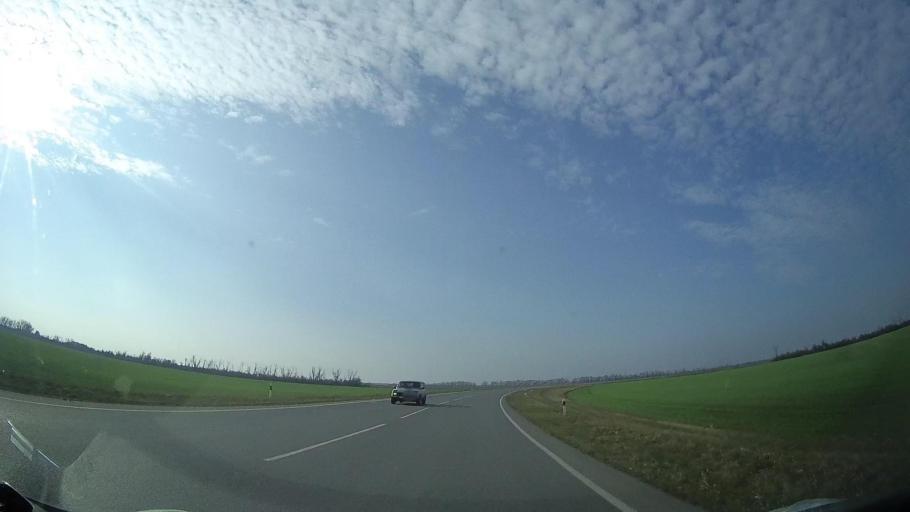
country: RU
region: Rostov
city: Tselina
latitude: 46.5149
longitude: 41.0702
